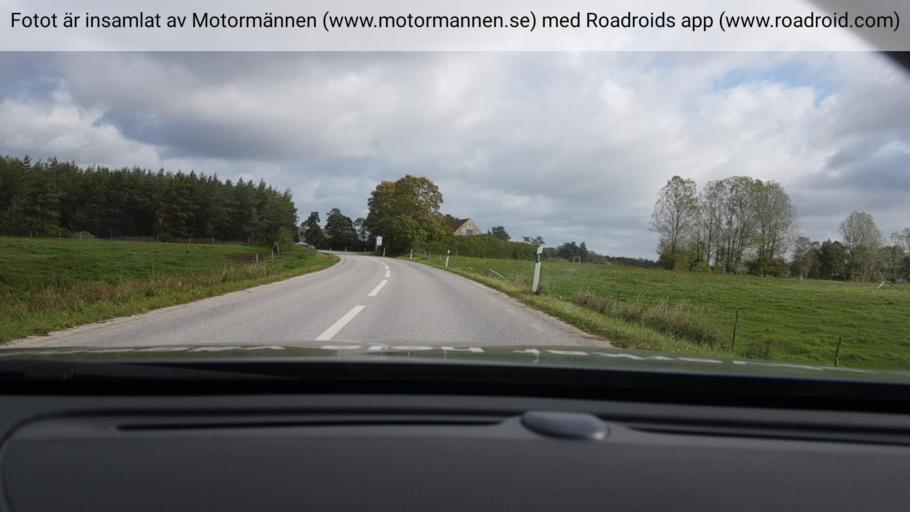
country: SE
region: Gotland
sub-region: Gotland
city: Visby
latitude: 57.6780
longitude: 18.4922
